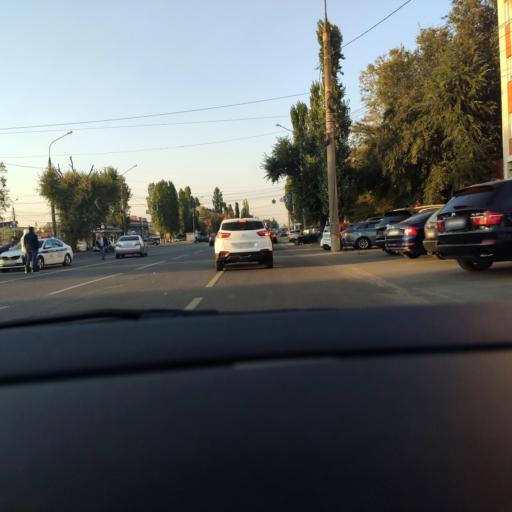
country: RU
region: Voronezj
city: Voronezh
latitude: 51.6807
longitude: 39.1664
